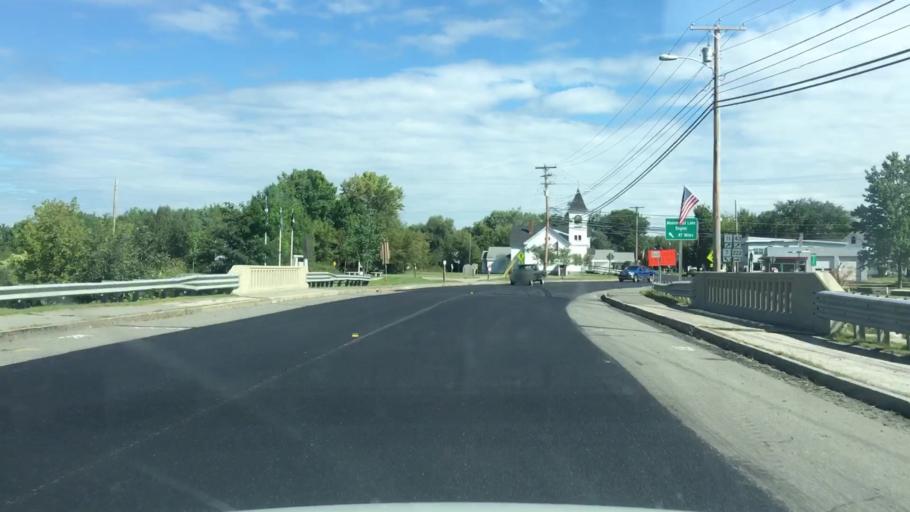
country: US
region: Maine
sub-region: Penobscot County
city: Corinna
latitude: 44.9210
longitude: -69.2603
